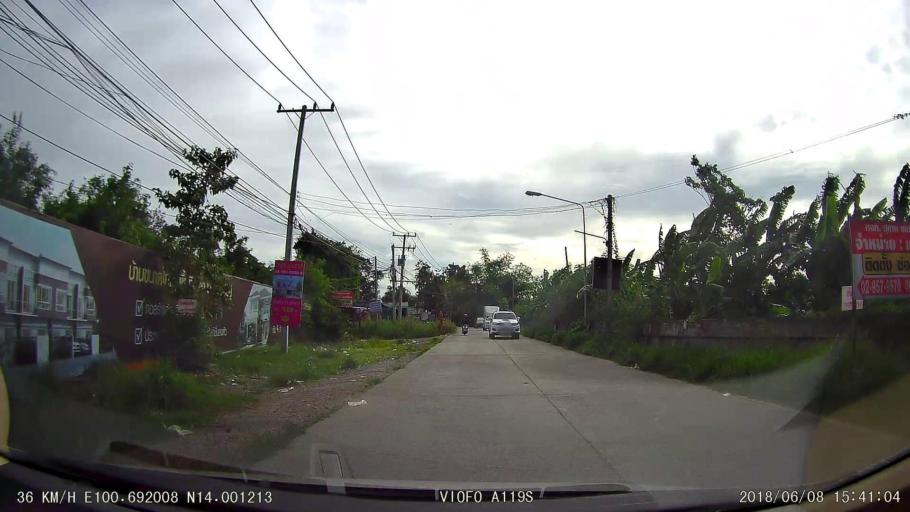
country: TH
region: Pathum Thani
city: Thanyaburi
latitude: 14.0012
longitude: 100.6919
